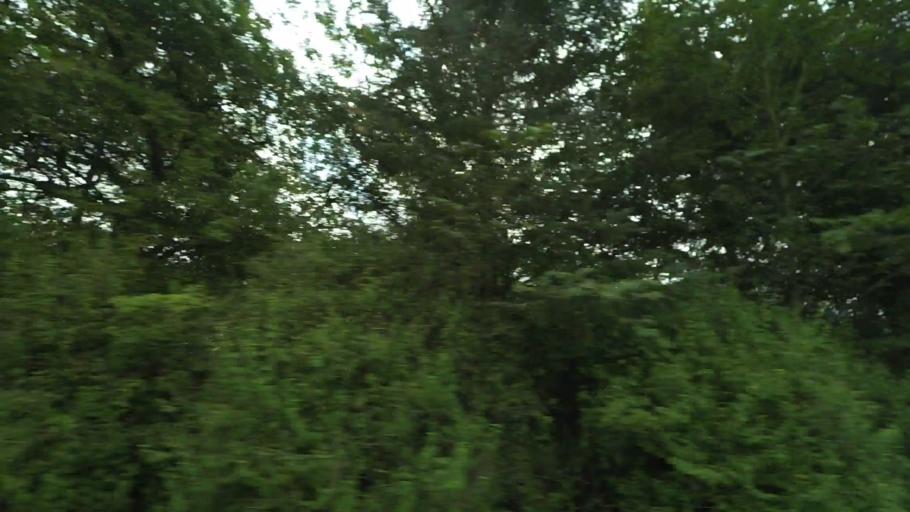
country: DK
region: Central Jutland
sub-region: Syddjurs Kommune
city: Ryomgard
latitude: 56.3981
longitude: 10.4896
